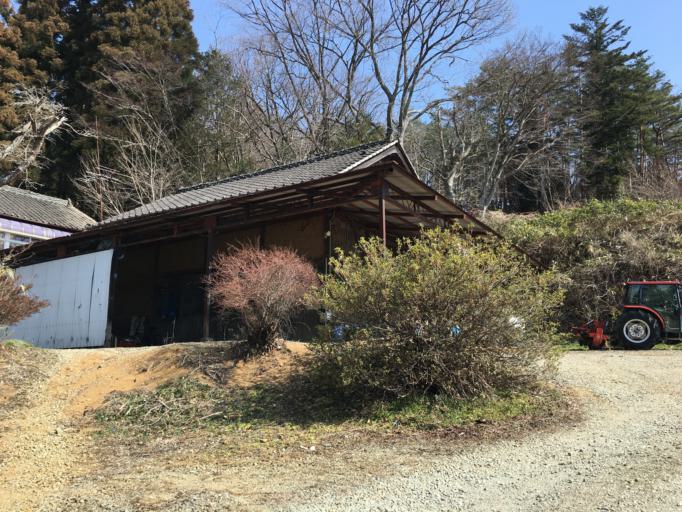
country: JP
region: Fukushima
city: Nihommatsu
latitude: 37.5905
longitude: 140.3780
